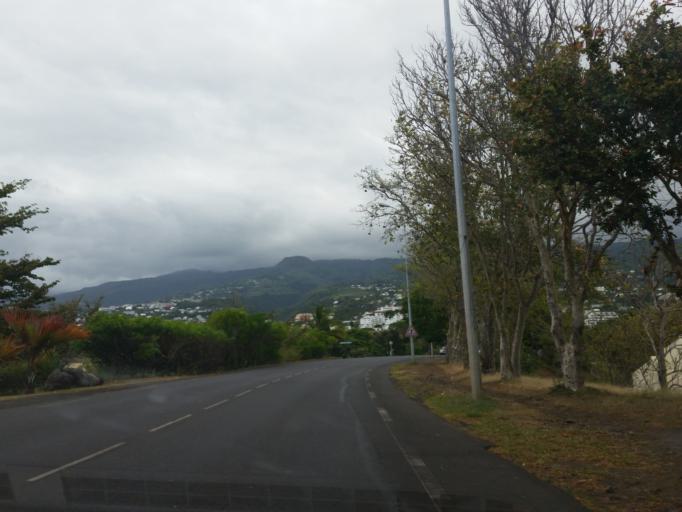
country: RE
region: Reunion
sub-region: Reunion
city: Saint-Denis
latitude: -20.8909
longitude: 55.4717
